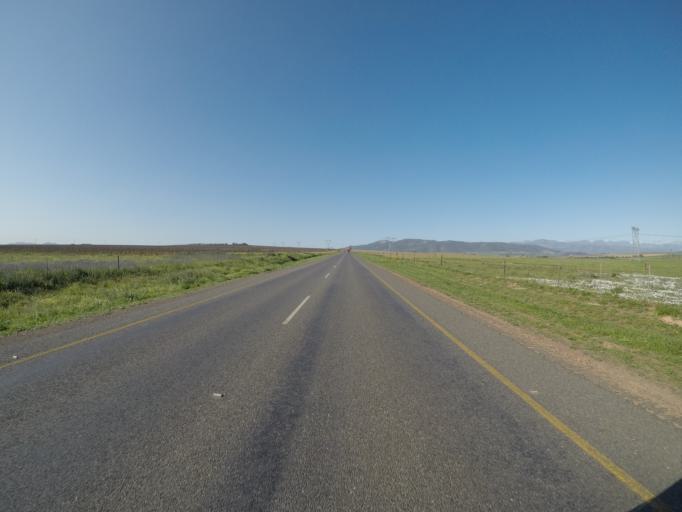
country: ZA
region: Western Cape
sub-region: City of Cape Town
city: Kraaifontein
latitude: -33.7567
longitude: 18.8146
